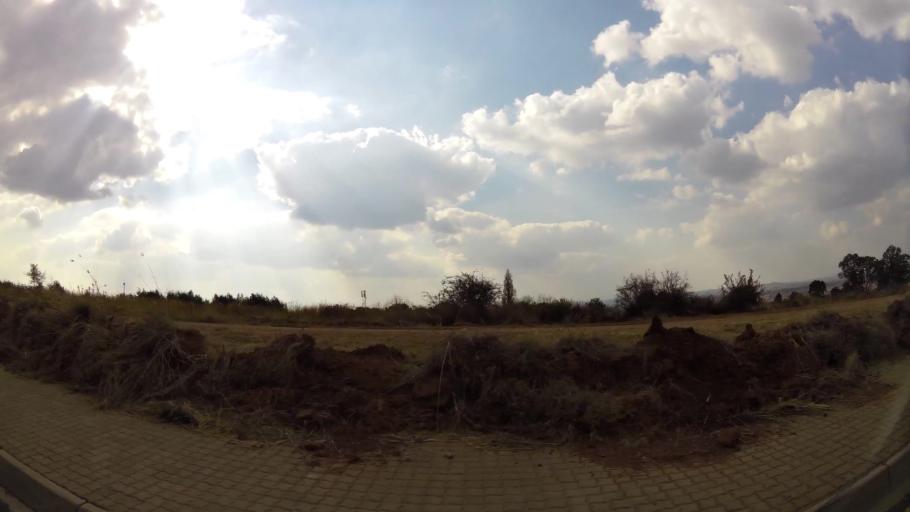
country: ZA
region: Gauteng
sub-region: City of Tshwane Metropolitan Municipality
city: Centurion
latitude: -25.9126
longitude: 28.1785
